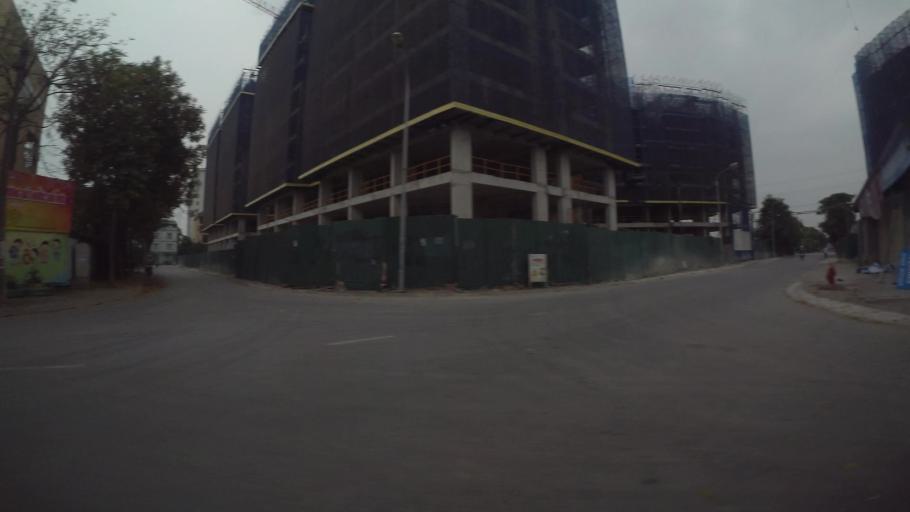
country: VN
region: Ha Noi
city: Trau Quy
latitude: 21.0369
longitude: 105.9081
